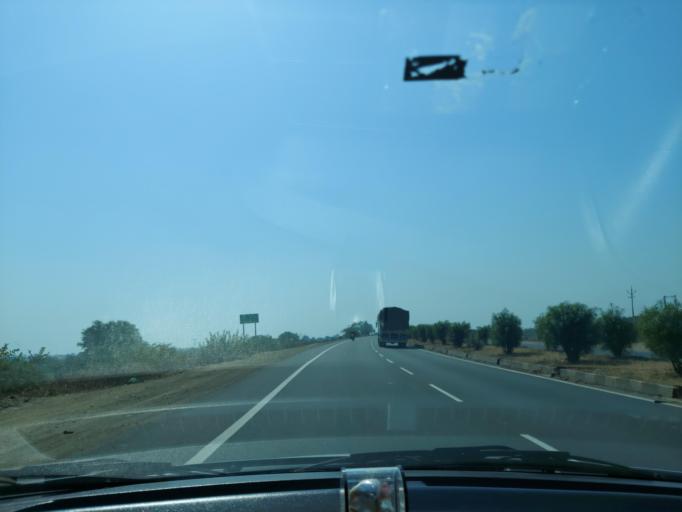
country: IN
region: Madhya Pradesh
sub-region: Dhar
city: Dhamnod
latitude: 22.3022
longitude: 75.5027
